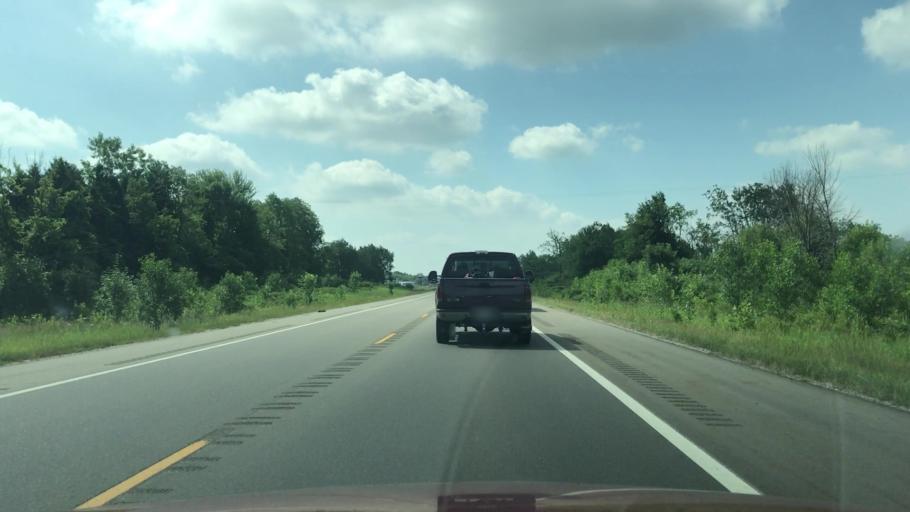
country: US
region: Michigan
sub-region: Kent County
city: Sparta
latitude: 43.1325
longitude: -85.7149
